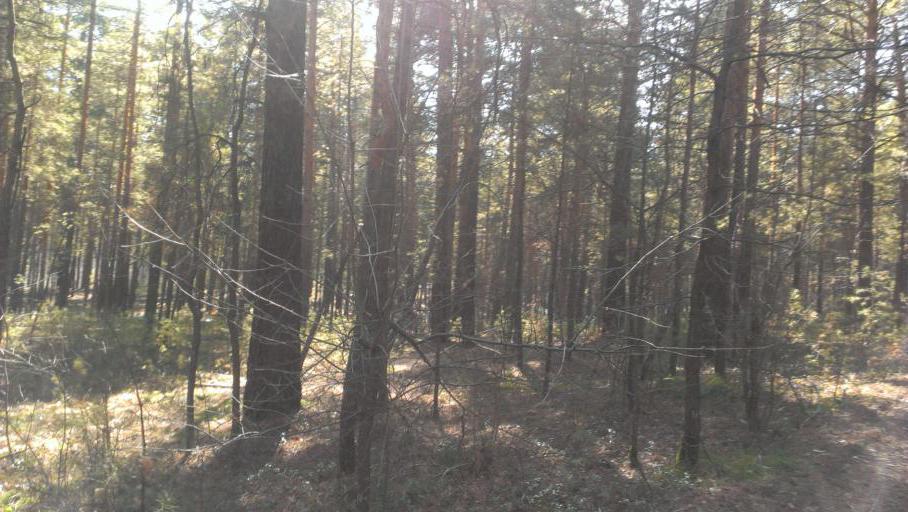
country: RU
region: Altai Krai
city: Yuzhnyy
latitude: 53.2976
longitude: 83.6971
